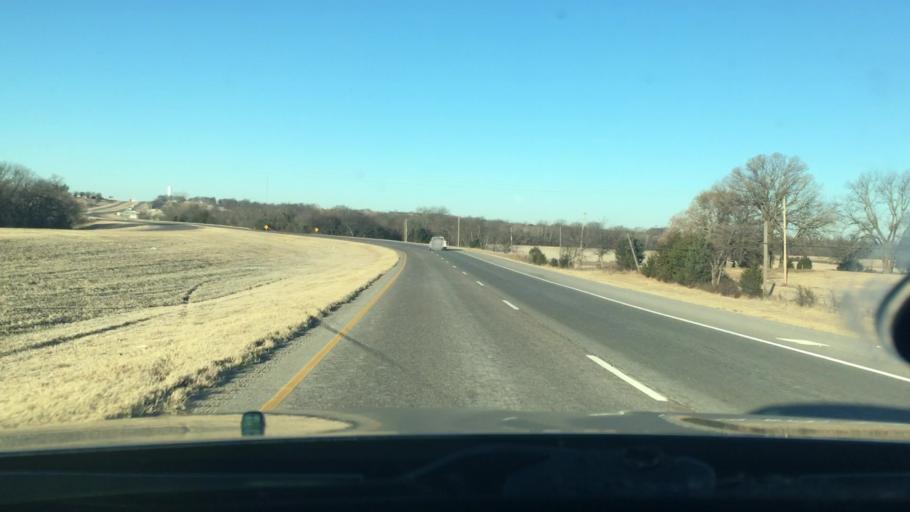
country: US
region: Oklahoma
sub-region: Murray County
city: Sulphur
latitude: 34.5071
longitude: -97.0277
